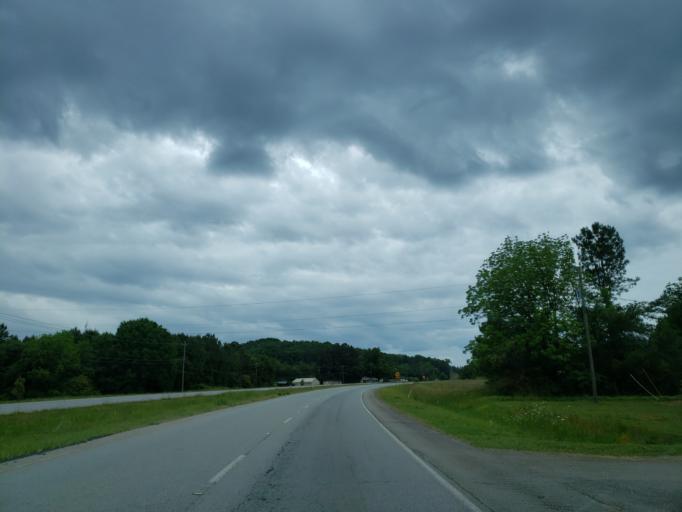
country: US
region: Georgia
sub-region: Polk County
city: Cedartown
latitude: 33.9445
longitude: -85.2436
